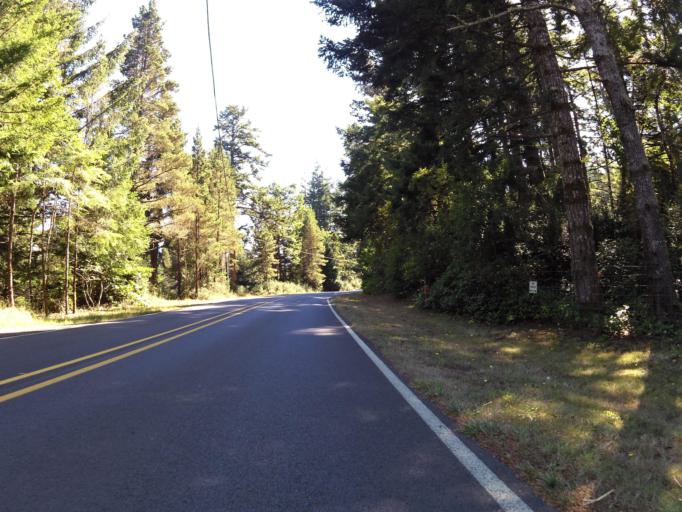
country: US
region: Oregon
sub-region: Coos County
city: Bandon
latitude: 43.2117
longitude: -124.3694
